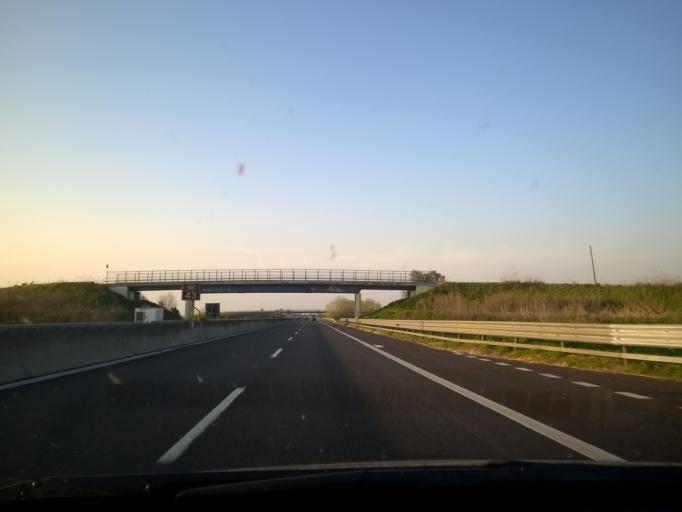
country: IT
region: Veneto
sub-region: Provincia di Rovigo
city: Occhiobello
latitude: 44.8909
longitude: 11.5702
